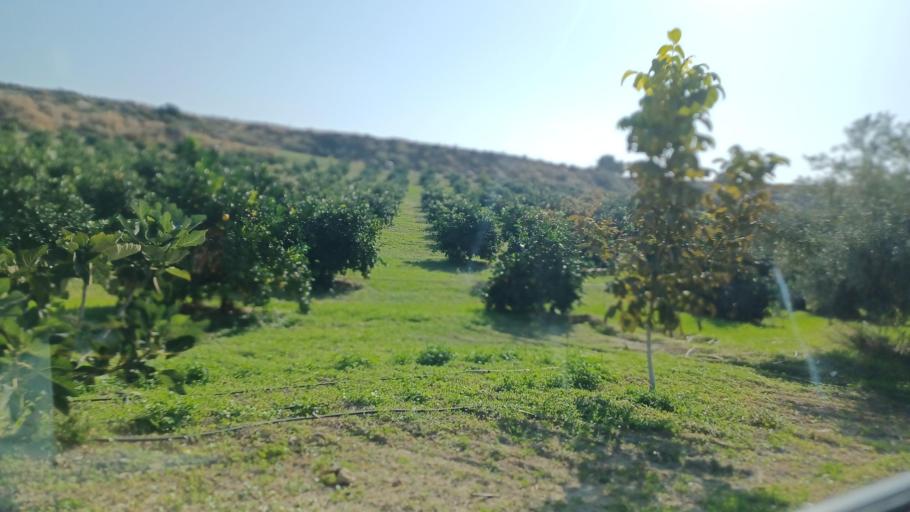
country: CY
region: Pafos
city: Polis
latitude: 35.0150
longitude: 32.4459
